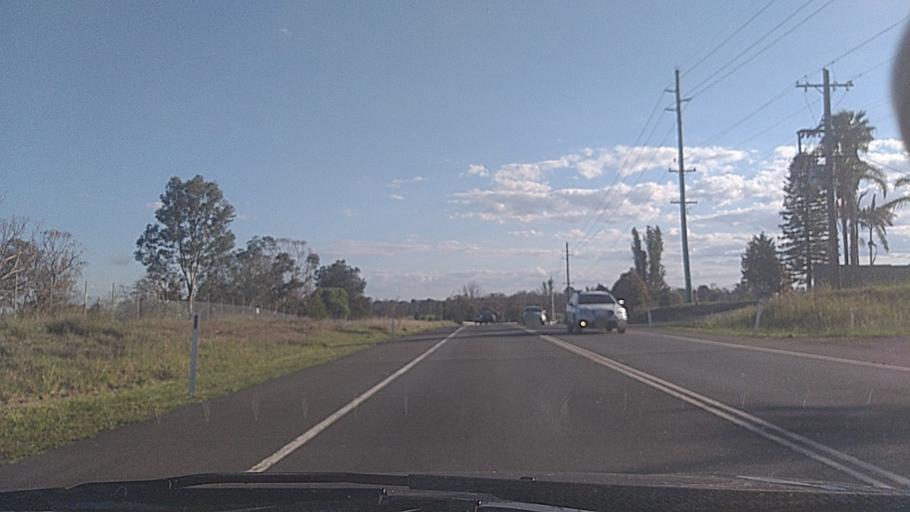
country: AU
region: New South Wales
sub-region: Penrith Municipality
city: Glenmore Park
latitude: -33.8166
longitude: 150.6885
